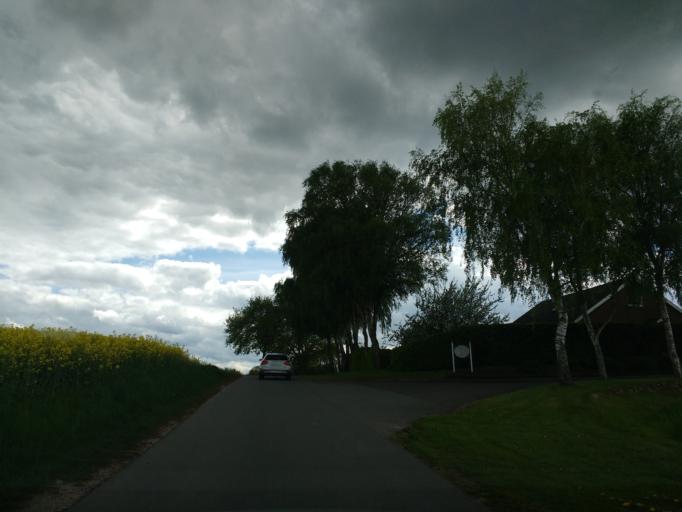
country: DE
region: Schleswig-Holstein
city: Loose
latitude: 54.5046
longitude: 9.8641
